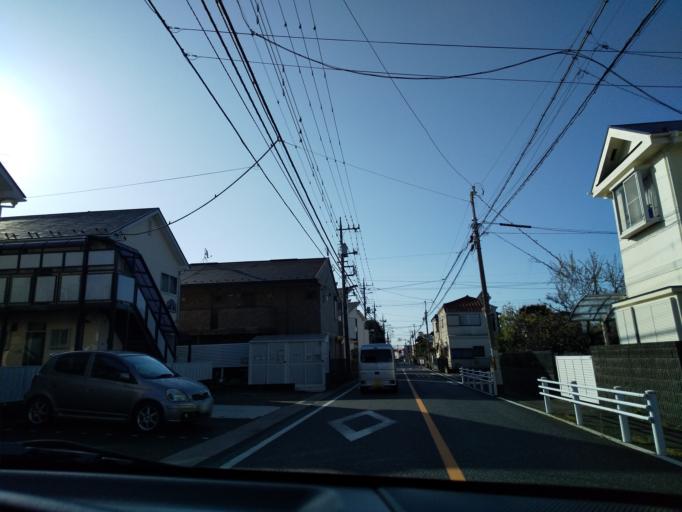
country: JP
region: Tokyo
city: Hino
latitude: 35.6956
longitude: 139.3984
